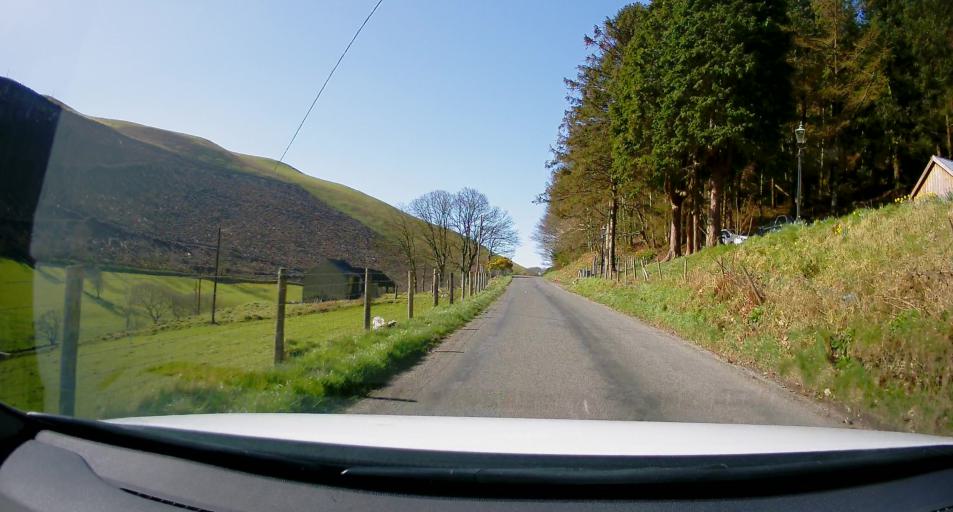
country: GB
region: Wales
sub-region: County of Ceredigion
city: Lledrod
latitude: 52.3510
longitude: -3.9096
